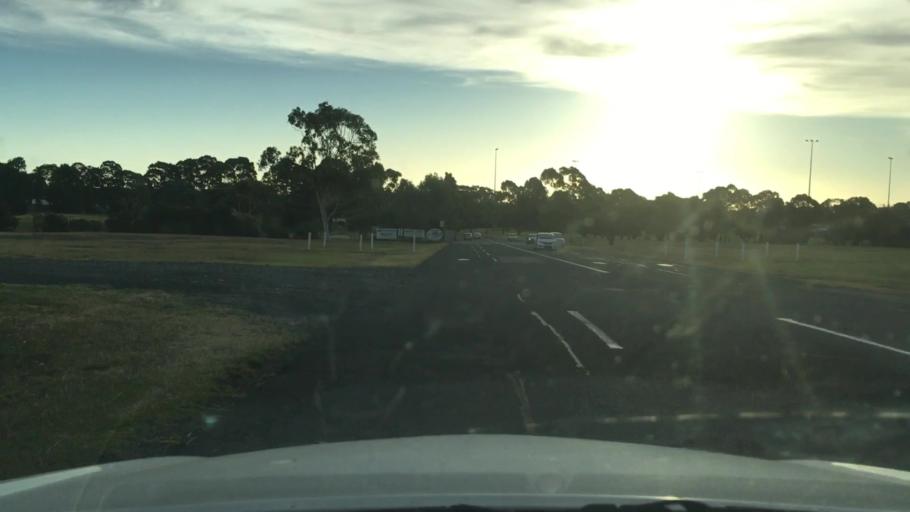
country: AU
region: Victoria
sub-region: Greater Dandenong
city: Springvale
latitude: -37.9452
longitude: 145.1657
